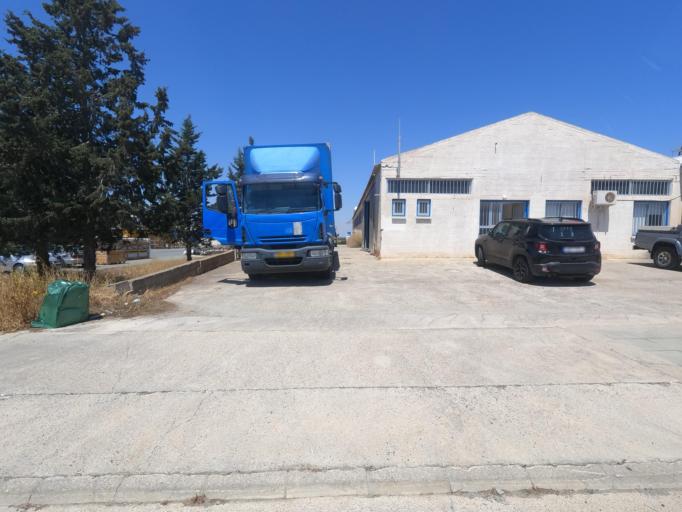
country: CY
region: Ammochostos
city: Frenaros
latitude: 35.0344
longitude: 33.9133
